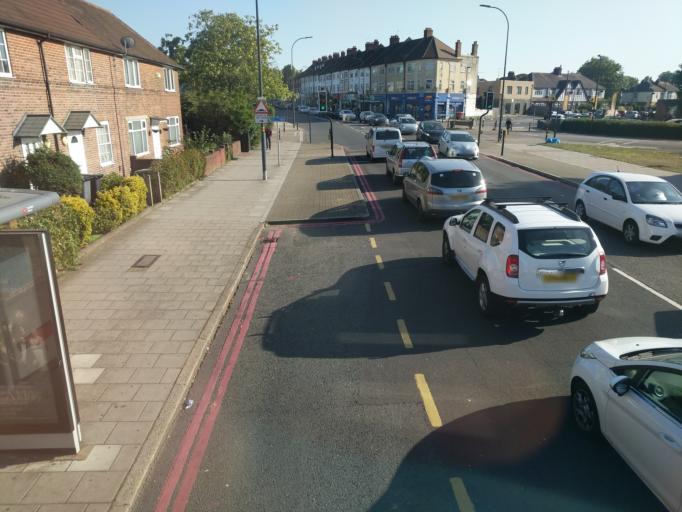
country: GB
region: England
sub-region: Greater London
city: Bromley
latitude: 51.4222
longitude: -0.0023
